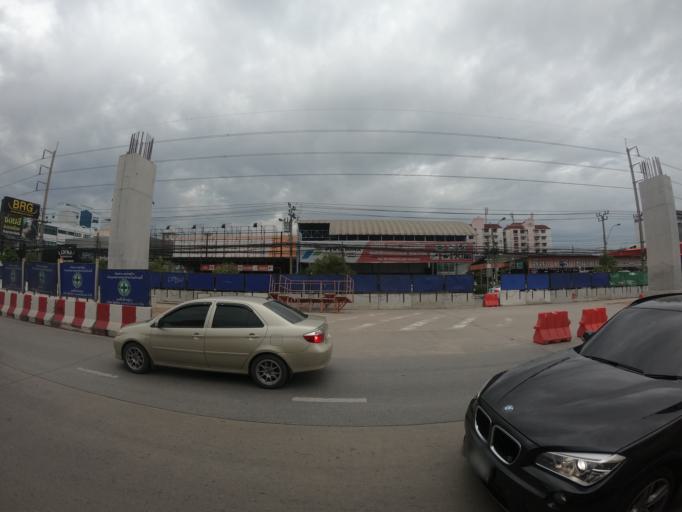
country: TH
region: Bangkok
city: Suan Luang
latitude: 13.7070
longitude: 100.6449
